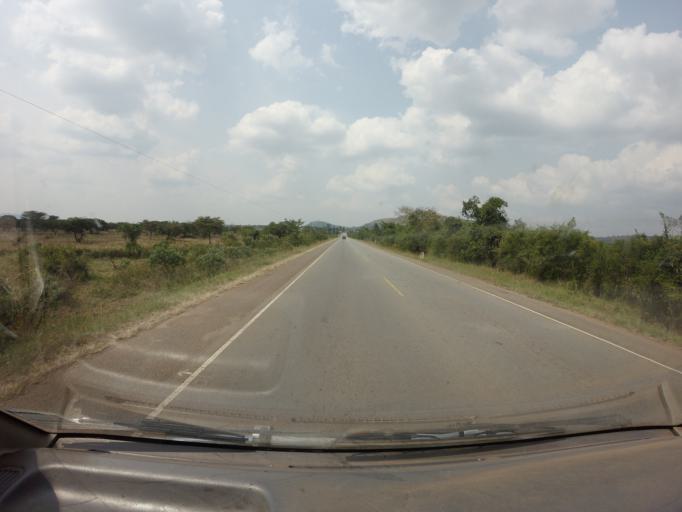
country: UG
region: Central Region
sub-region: Lyantonde District
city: Lyantonde
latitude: -0.3951
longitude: 31.1770
